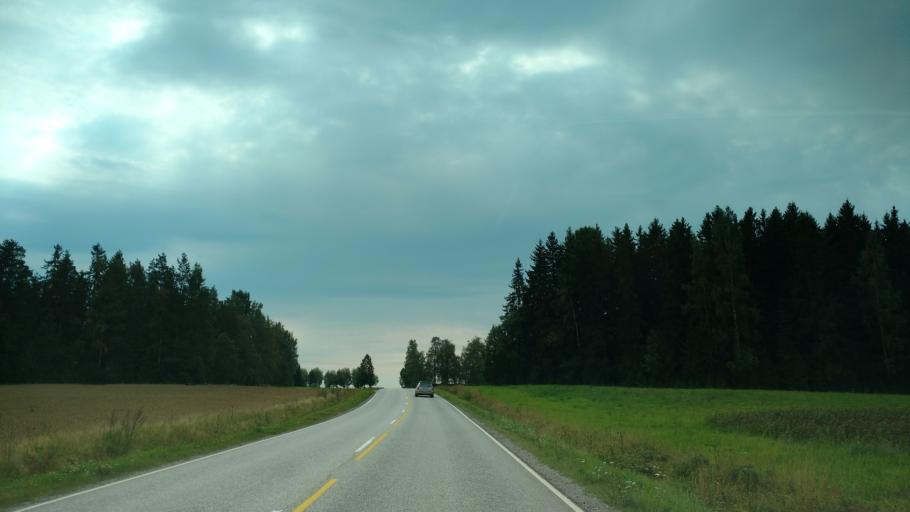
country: FI
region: Varsinais-Suomi
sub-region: Salo
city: Kuusjoki
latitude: 60.4672
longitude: 23.1607
